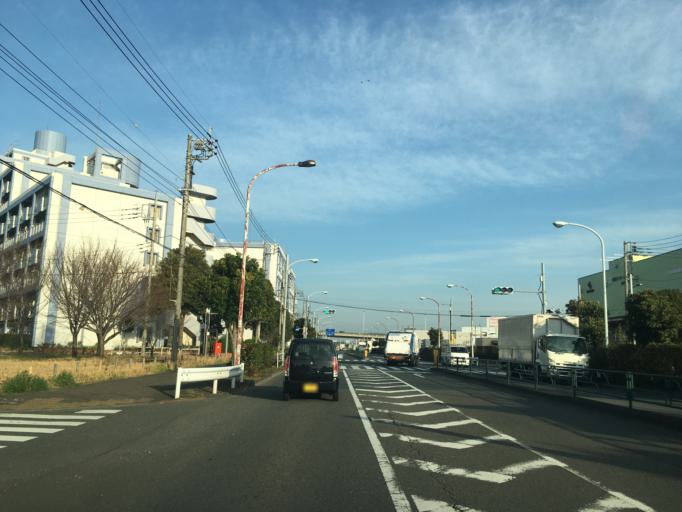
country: JP
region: Tokyo
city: Hino
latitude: 35.6734
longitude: 139.4325
